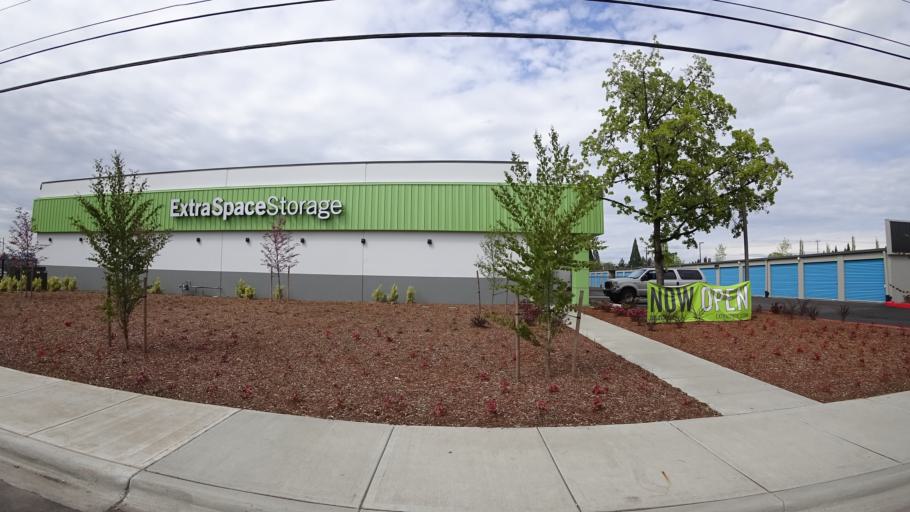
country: US
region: Oregon
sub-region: Washington County
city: Hillsboro
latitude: 45.4997
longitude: -122.9344
